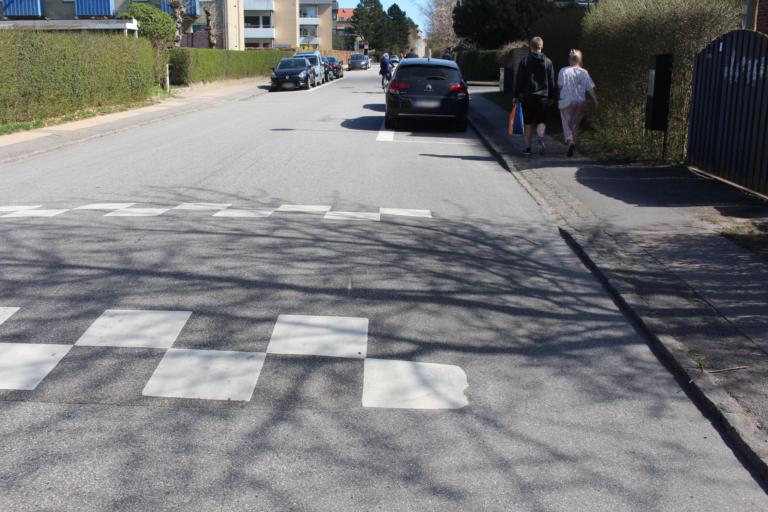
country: DK
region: Capital Region
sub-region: Kobenhavn
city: Vanlose
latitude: 55.6825
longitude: 12.4777
